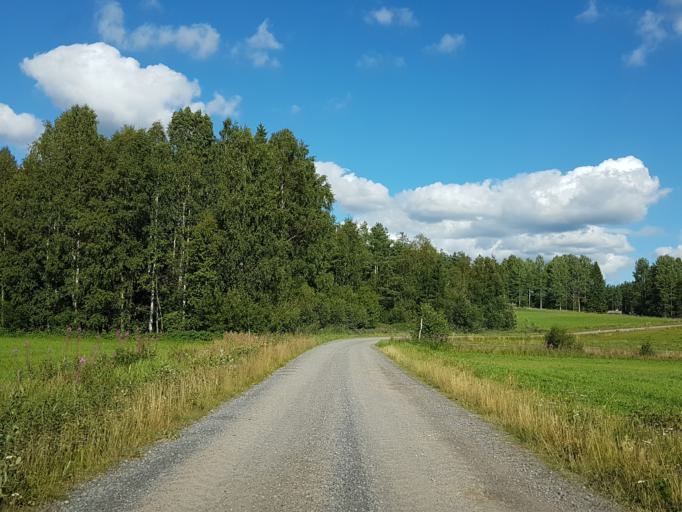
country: SE
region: Vaesterbotten
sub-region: Skelleftea Kommun
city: Burtraesk
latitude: 64.2966
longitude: 20.4789
